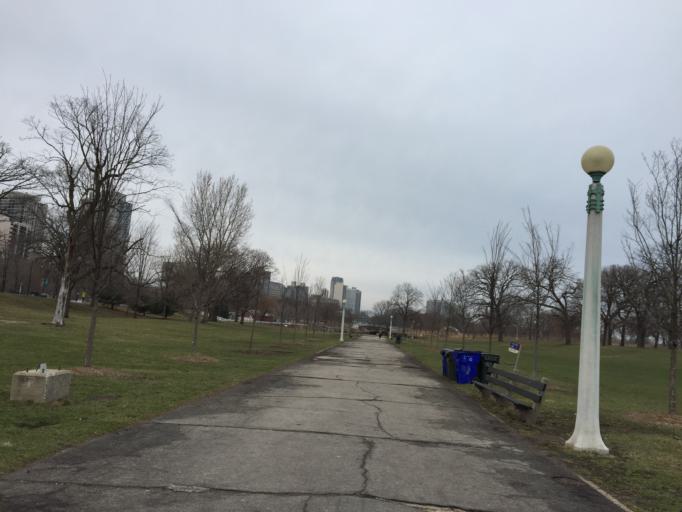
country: US
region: Illinois
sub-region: Cook County
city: Chicago
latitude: 41.9148
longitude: -87.6316
